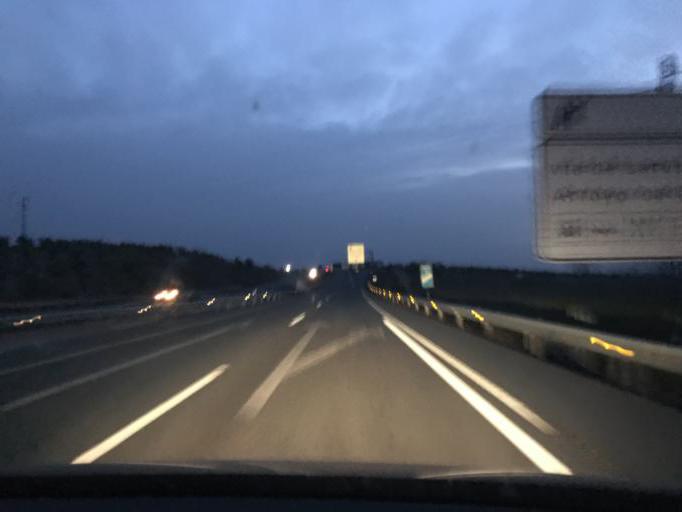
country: ES
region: Andalusia
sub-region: Provincia de Granada
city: Gor
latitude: 37.3976
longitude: -2.9827
